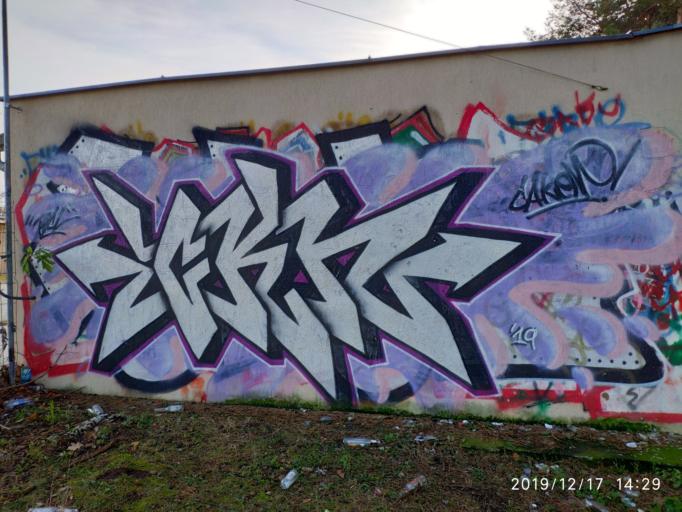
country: PL
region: Lubusz
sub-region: Zielona Gora
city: Zielona Gora
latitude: 51.9465
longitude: 15.4704
